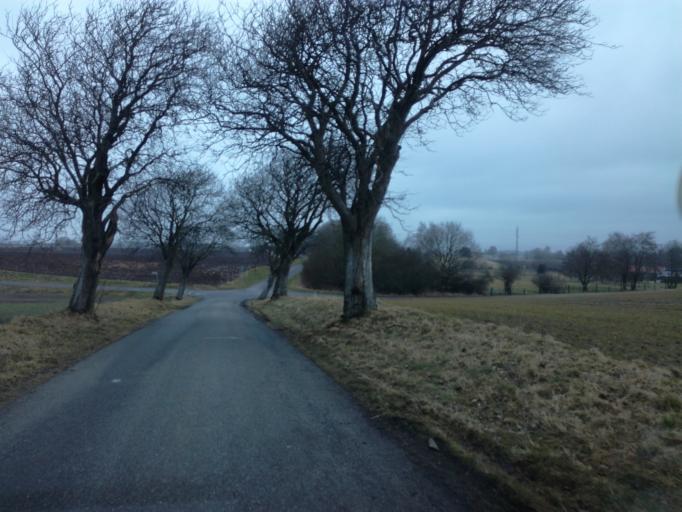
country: DK
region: South Denmark
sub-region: Vejle Kommune
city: Brejning
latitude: 55.6242
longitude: 9.7118
